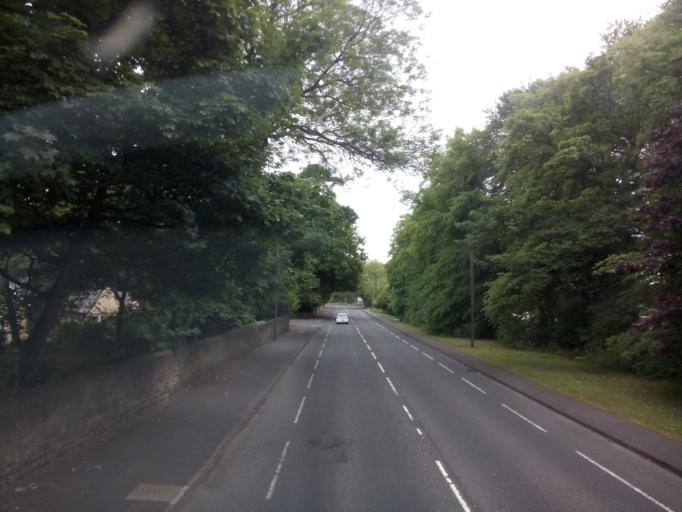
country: GB
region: England
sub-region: County Durham
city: Chester-le-Street
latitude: 54.8732
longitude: -1.5755
